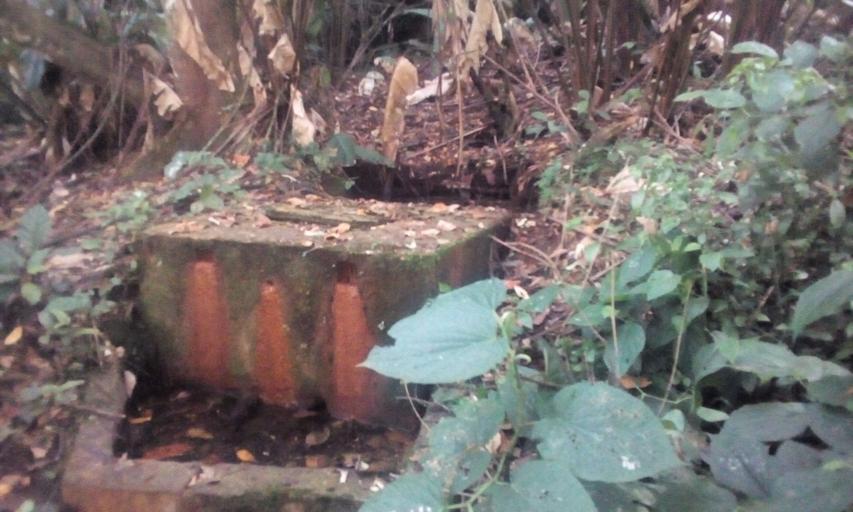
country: CO
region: Boyaca
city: Santana
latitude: 6.0015
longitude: -73.5020
